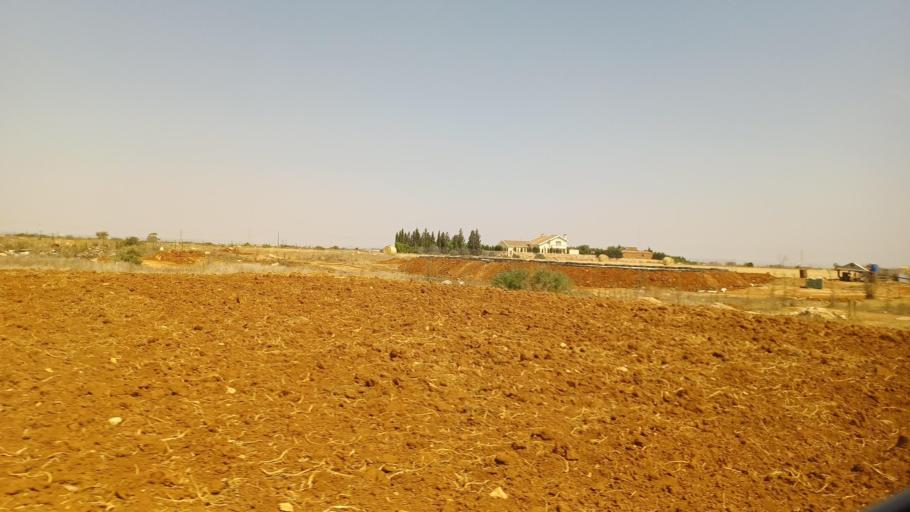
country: CY
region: Ammochostos
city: Frenaros
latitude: 35.0626
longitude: 33.9106
